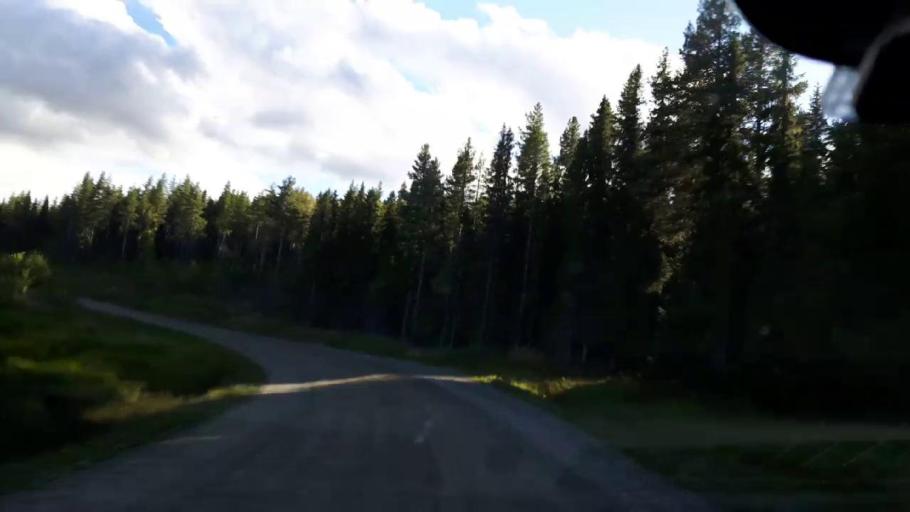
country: SE
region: Jaemtland
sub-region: Stroemsunds Kommun
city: Stroemsund
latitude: 63.3429
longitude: 15.5671
